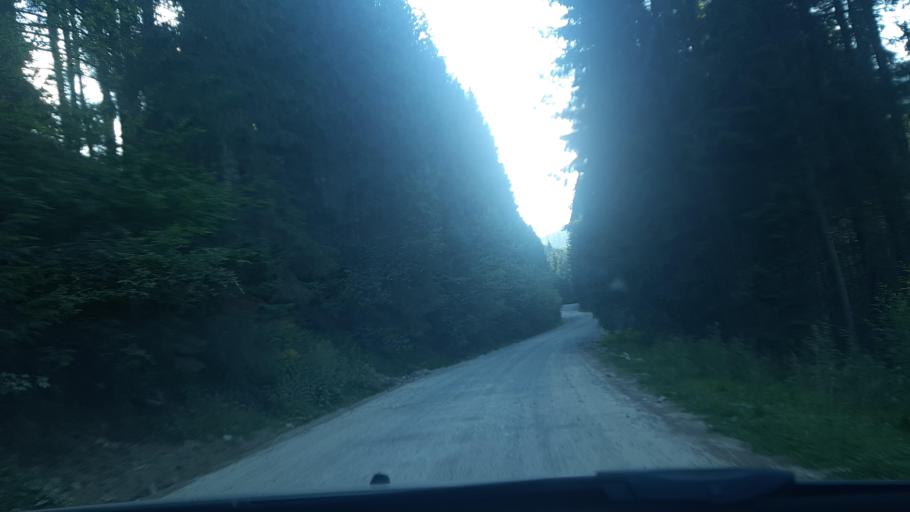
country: RO
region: Alba
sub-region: Comuna Sugag
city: Sugag
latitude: 45.5753
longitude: 23.6091
